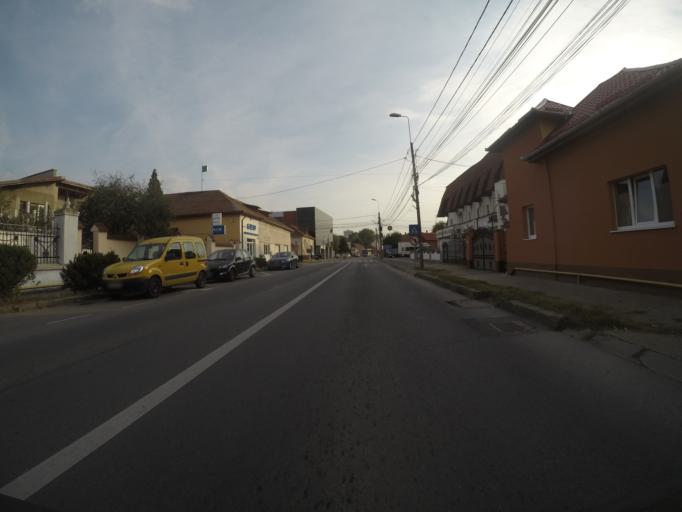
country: RO
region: Alba
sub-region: Municipiul Alba Iulia
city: Alba Iulia
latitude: 46.0602
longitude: 23.5768
